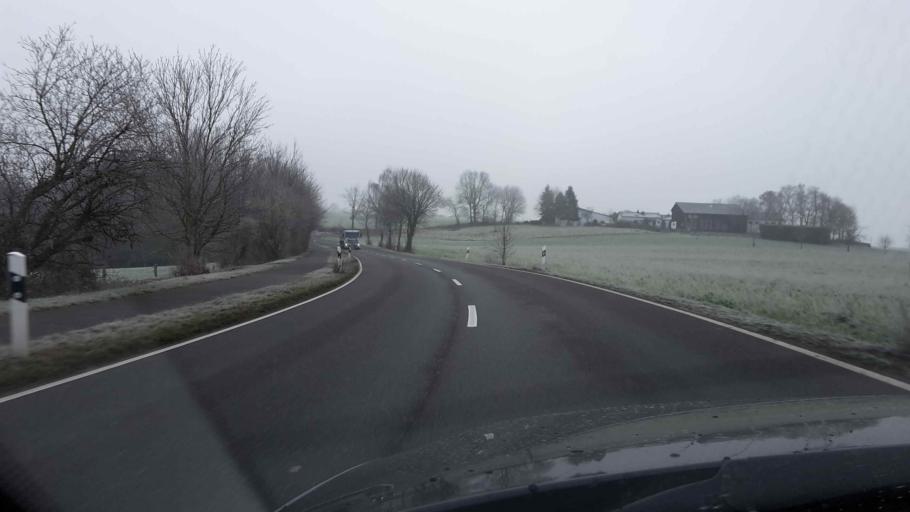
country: DE
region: North Rhine-Westphalia
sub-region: Regierungsbezirk Koln
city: Hennef
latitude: 50.7396
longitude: 7.2846
